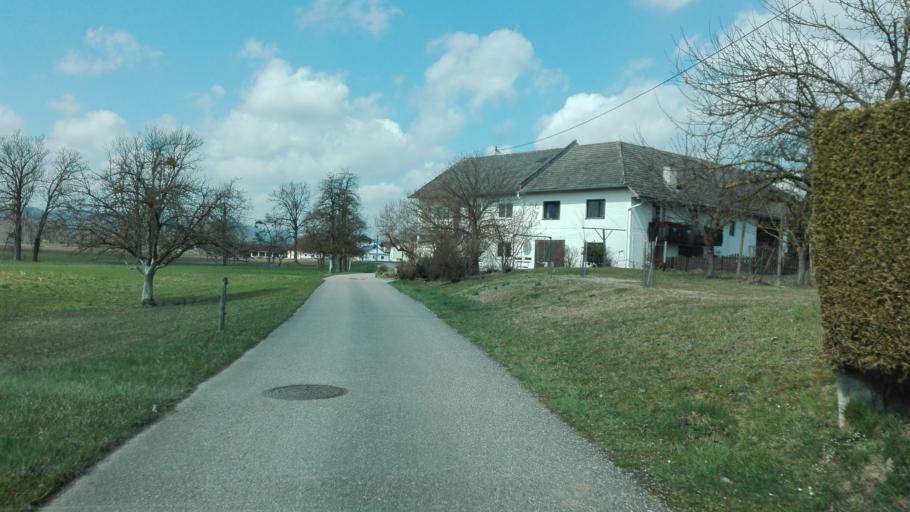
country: AT
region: Upper Austria
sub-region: Politischer Bezirk Urfahr-Umgebung
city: Feldkirchen an der Donau
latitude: 48.3388
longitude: 14.0512
